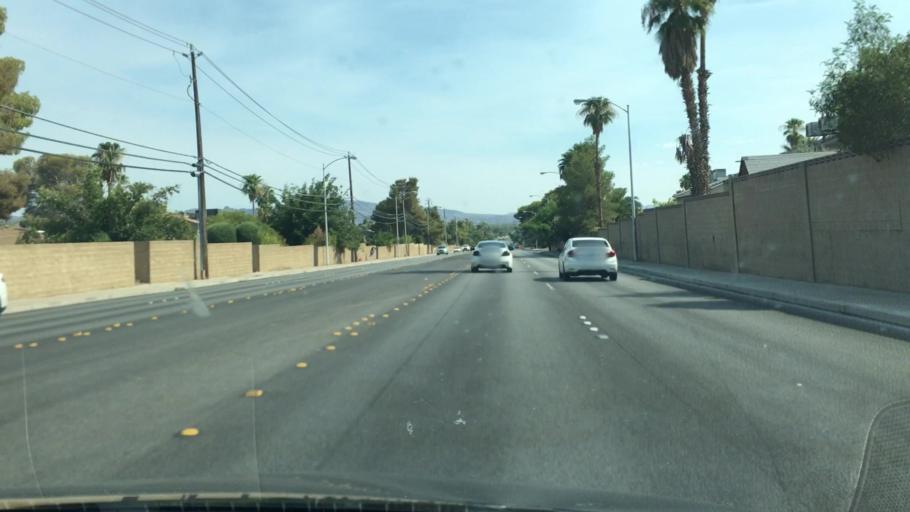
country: US
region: Nevada
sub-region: Clark County
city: Whitney
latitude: 36.0965
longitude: -115.0917
